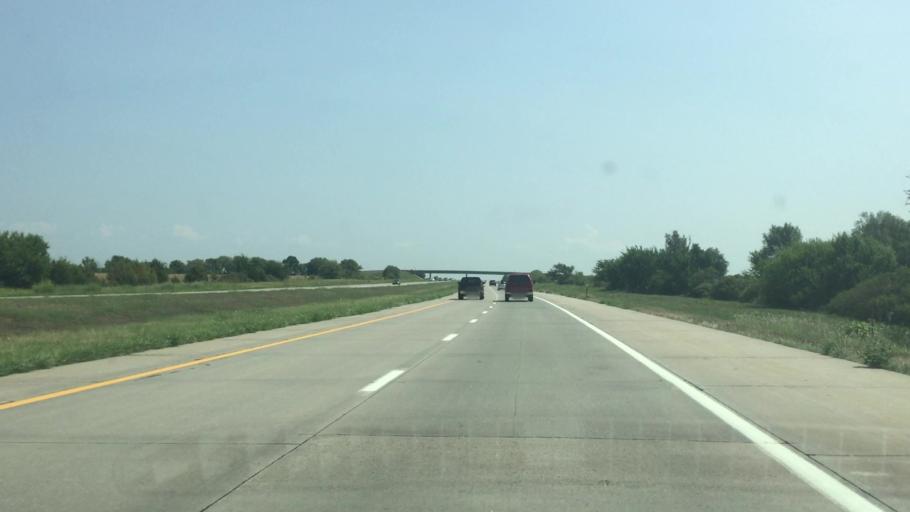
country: US
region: Kansas
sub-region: Osage County
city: Lyndon
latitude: 38.4592
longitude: -95.5514
